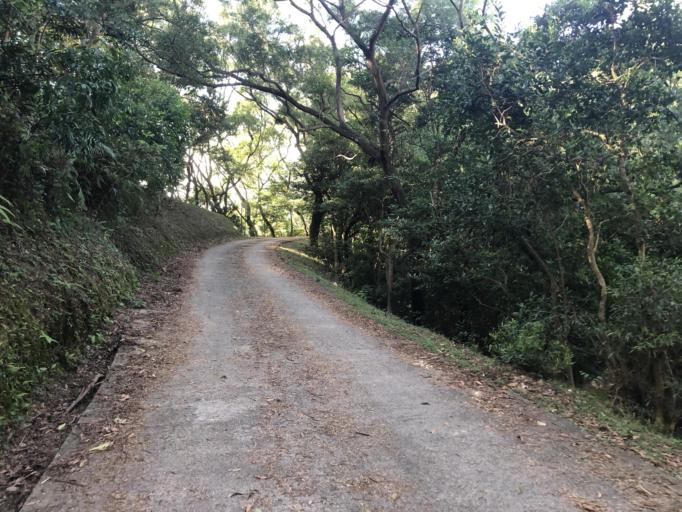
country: HK
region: Tsuen Wan
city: Tsuen Wan
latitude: 22.3926
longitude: 114.0856
